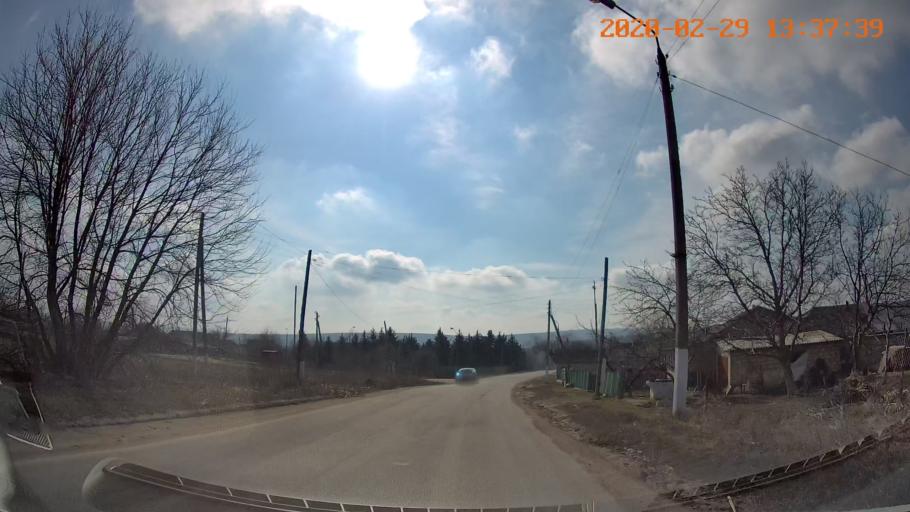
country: MD
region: Telenesti
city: Camenca
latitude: 47.8614
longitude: 28.6013
